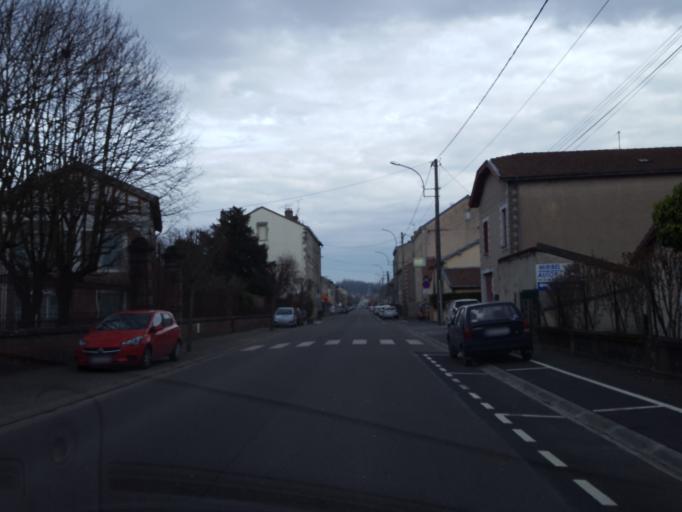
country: FR
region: Lorraine
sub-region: Departement de la Meuse
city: Verdun
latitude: 49.1677
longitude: 5.3916
